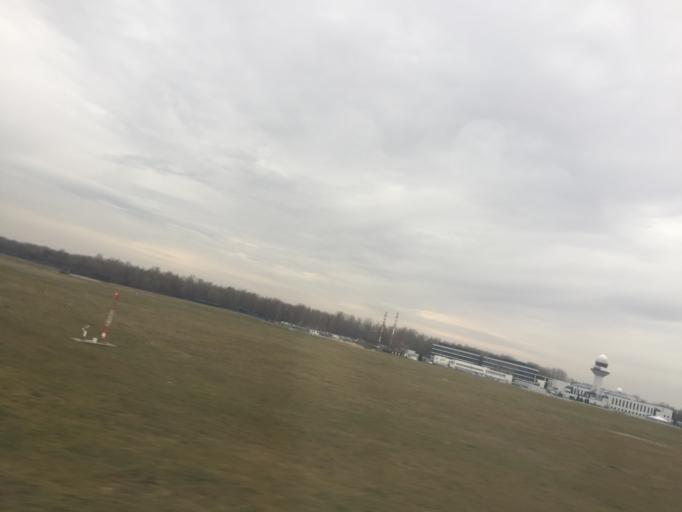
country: PL
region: Masovian Voivodeship
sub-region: Warszawa
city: Wlochy
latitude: 52.1661
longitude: 20.9659
